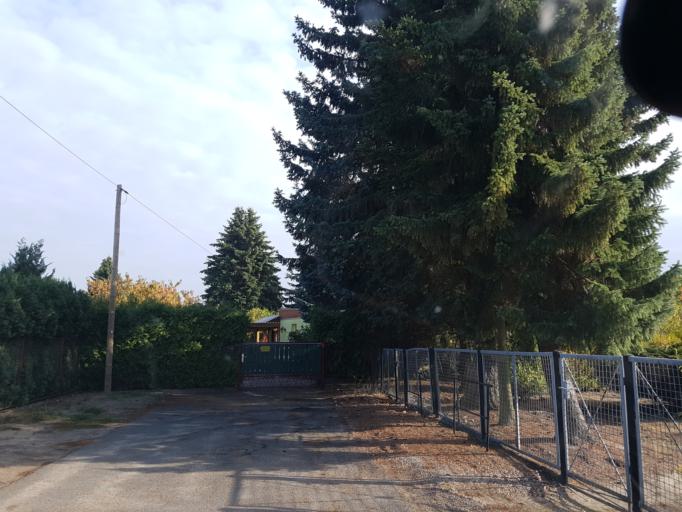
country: DE
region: Brandenburg
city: Finsterwalde
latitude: 51.6204
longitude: 13.7205
